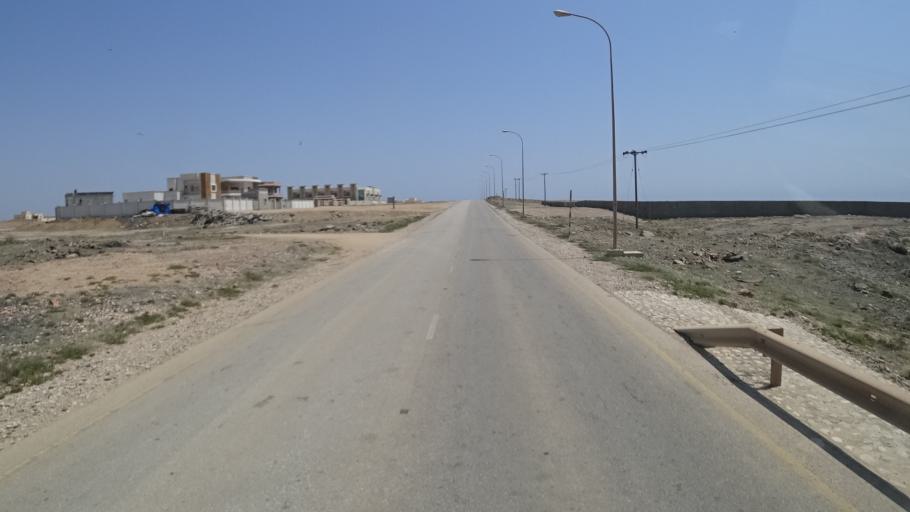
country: OM
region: Zufar
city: Salalah
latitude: 16.9762
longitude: 54.7134
